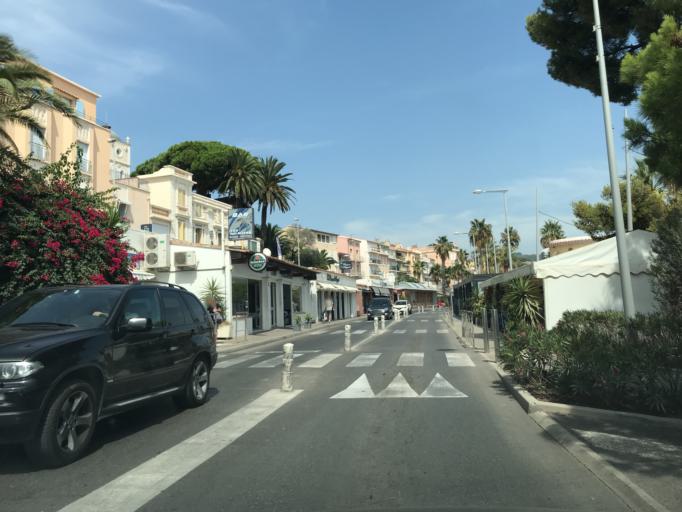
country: FR
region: Provence-Alpes-Cote d'Azur
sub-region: Departement du Var
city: Bandol
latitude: 43.1337
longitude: 5.7521
